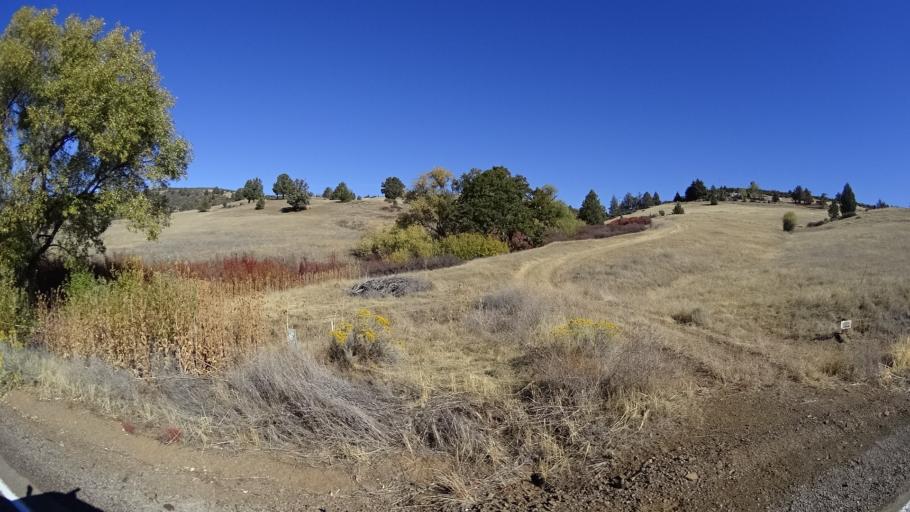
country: US
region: California
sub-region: Siskiyou County
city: Montague
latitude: 41.8657
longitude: -122.4442
